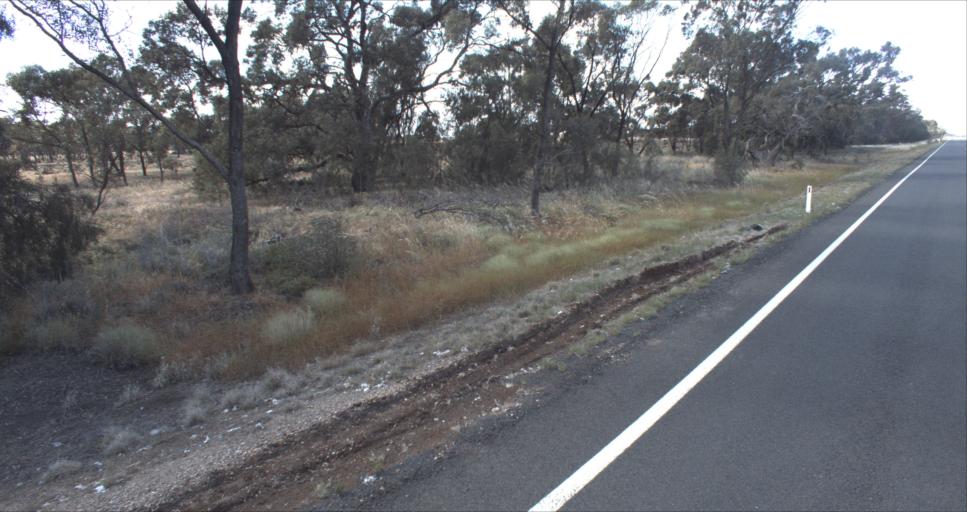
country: AU
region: New South Wales
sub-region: Murrumbidgee Shire
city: Darlington Point
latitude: -34.5312
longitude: 146.1739
